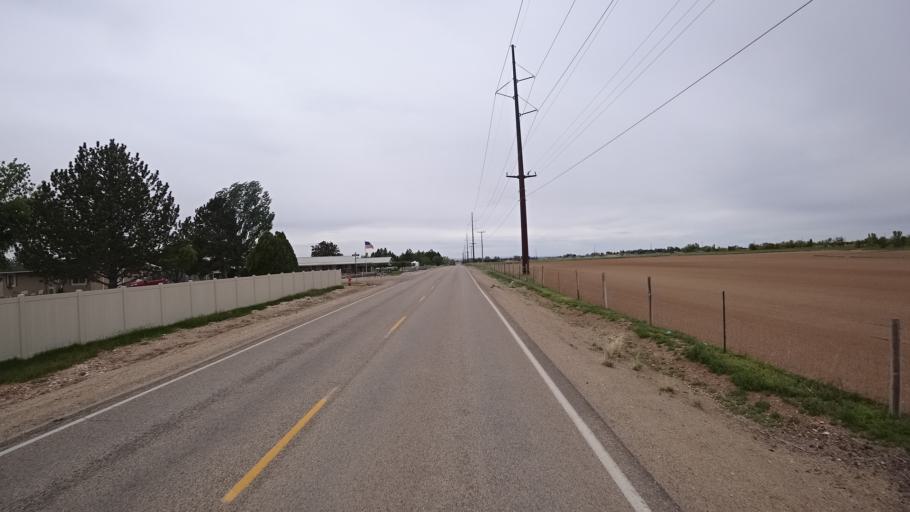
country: US
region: Idaho
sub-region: Ada County
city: Kuna
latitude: 43.4883
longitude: -116.3226
